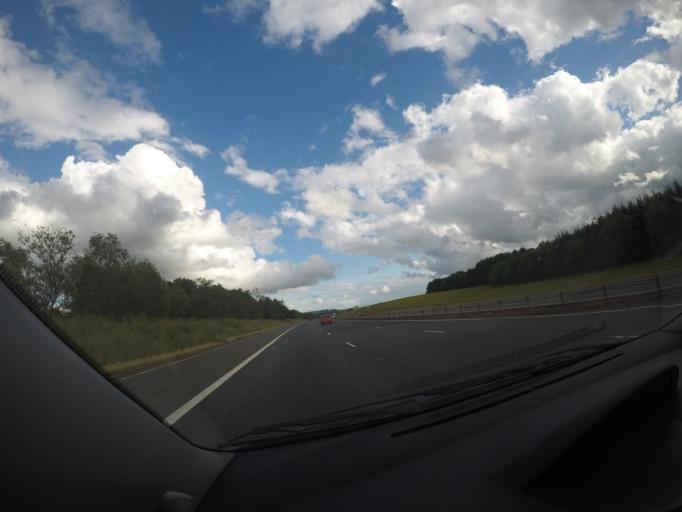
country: GB
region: Scotland
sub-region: Dumfries and Galloway
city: Lockerbie
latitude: 55.1718
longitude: -3.3946
